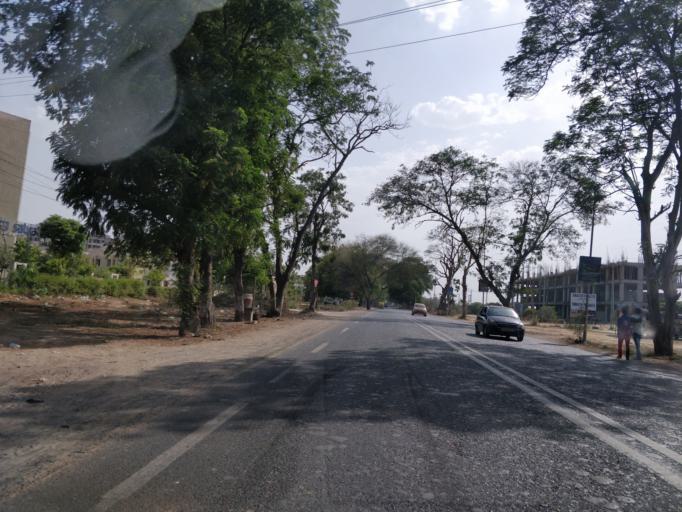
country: IN
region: Gujarat
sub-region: Ahmadabad
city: Naroda
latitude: 23.0864
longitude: 72.6825
